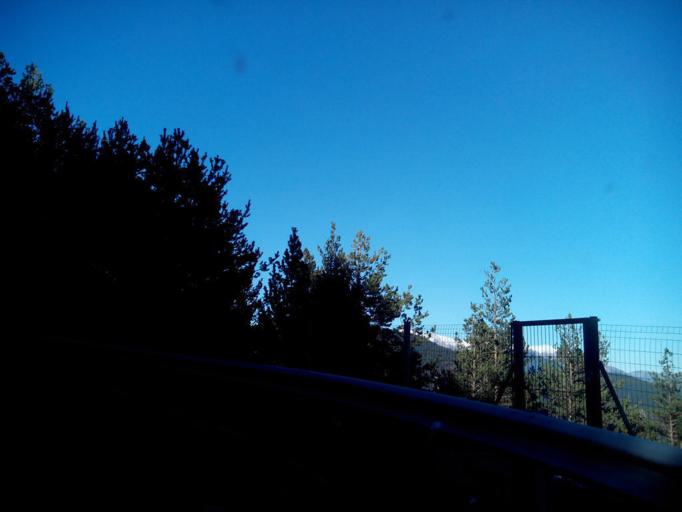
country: ES
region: Catalonia
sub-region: Provincia de Barcelona
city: Saldes
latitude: 42.2459
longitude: 1.7212
